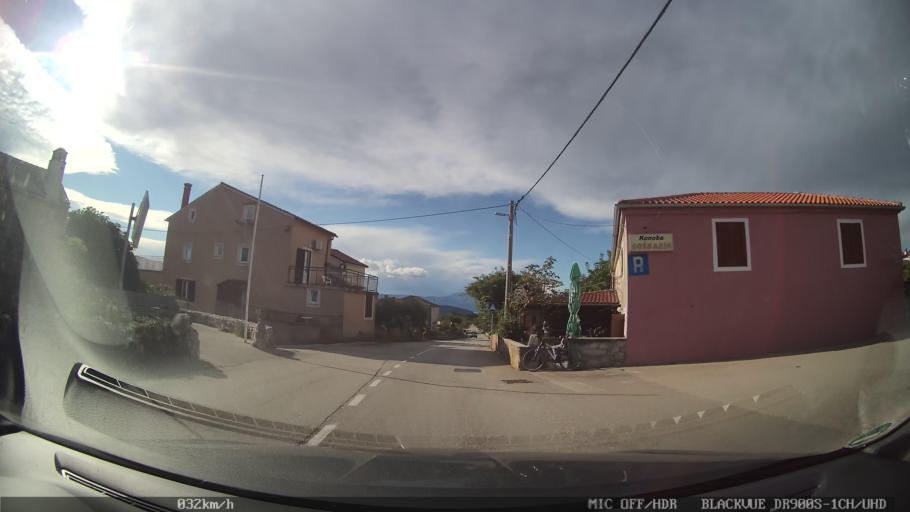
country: HR
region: Primorsko-Goranska
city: Njivice
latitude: 45.0734
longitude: 14.4652
